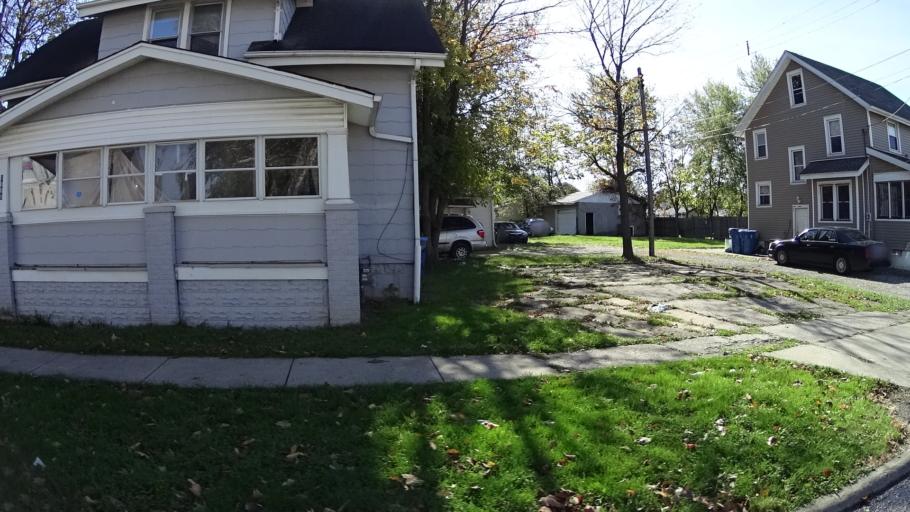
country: US
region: Ohio
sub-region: Lorain County
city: Lorain
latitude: 41.4535
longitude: -82.1797
